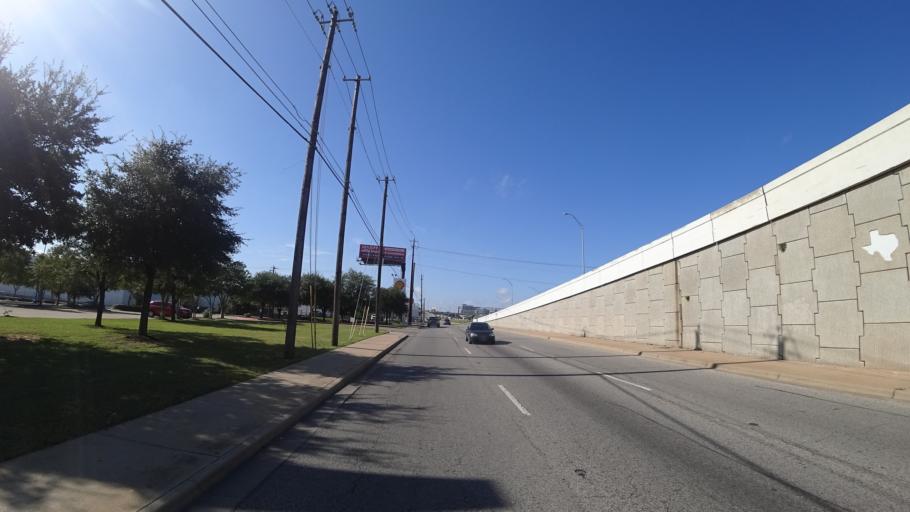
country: US
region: Texas
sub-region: Travis County
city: Austin
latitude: 30.3368
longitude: -97.7010
